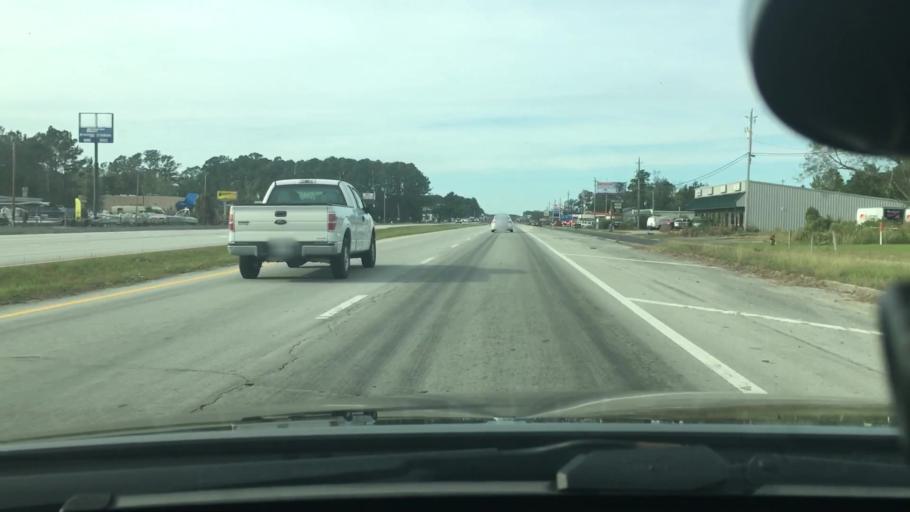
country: US
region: North Carolina
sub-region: Craven County
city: Havelock
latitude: 34.8969
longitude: -76.9277
